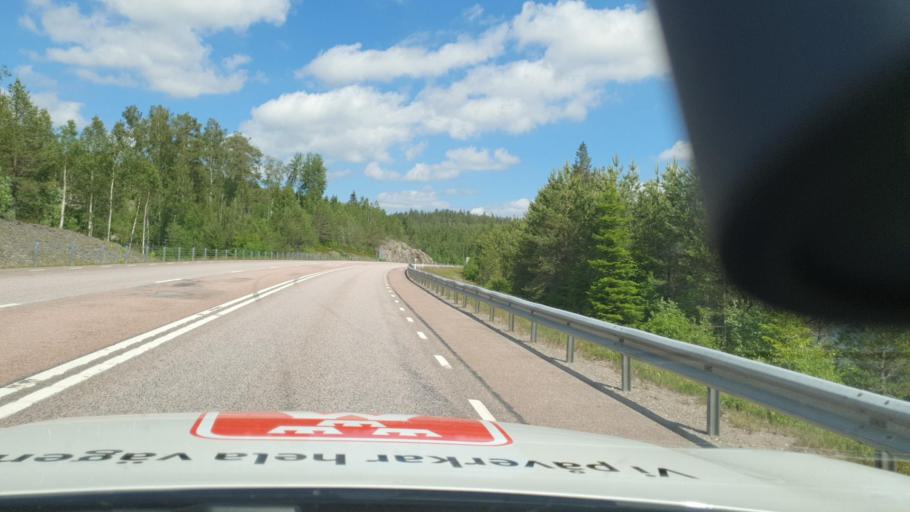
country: SE
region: Vaermland
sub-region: Filipstads Kommun
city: Filipstad
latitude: 59.6929
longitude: 14.0862
